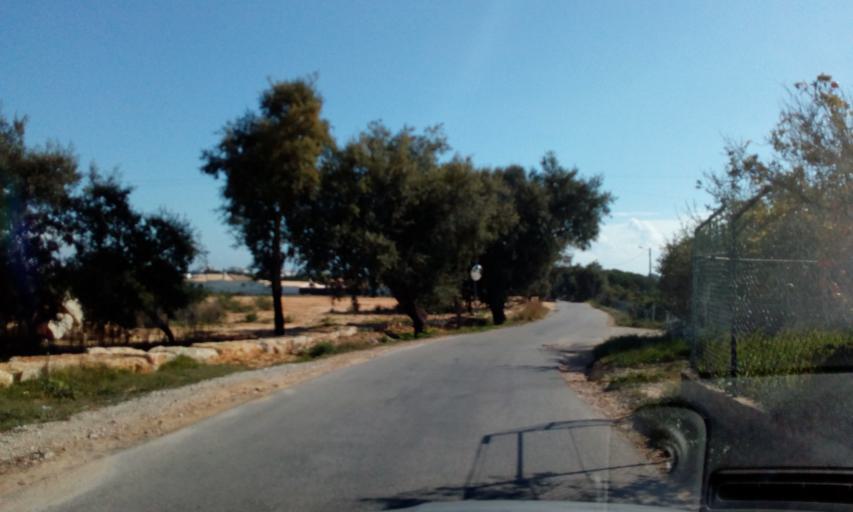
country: PT
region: Faro
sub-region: Albufeira
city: Ferreiras
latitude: 37.0993
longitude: -8.2051
